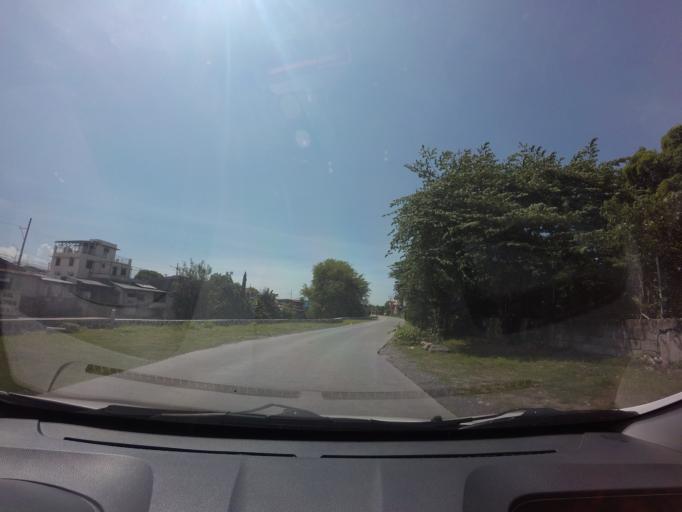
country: PH
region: Calabarzon
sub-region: Province of Rizal
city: Las Pinas
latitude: 14.4468
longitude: 120.9701
